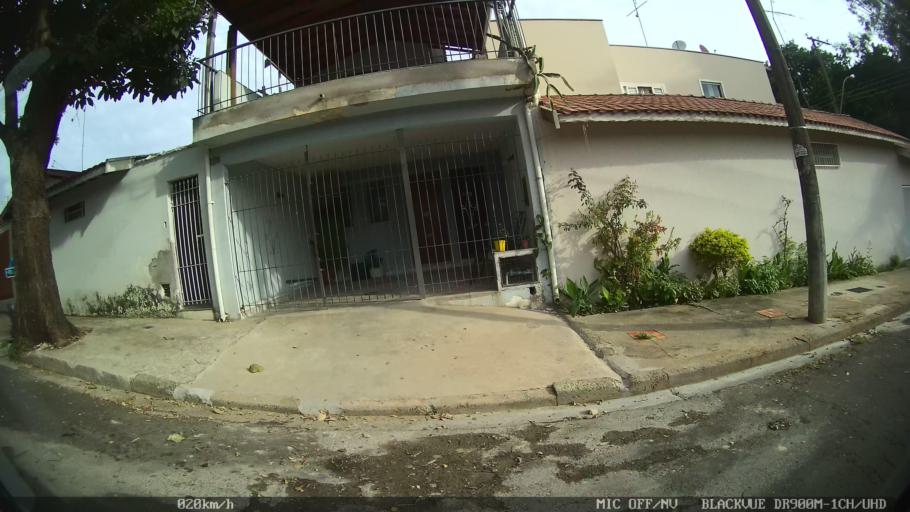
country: BR
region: Sao Paulo
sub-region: Piracicaba
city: Piracicaba
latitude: -22.7373
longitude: -47.6251
